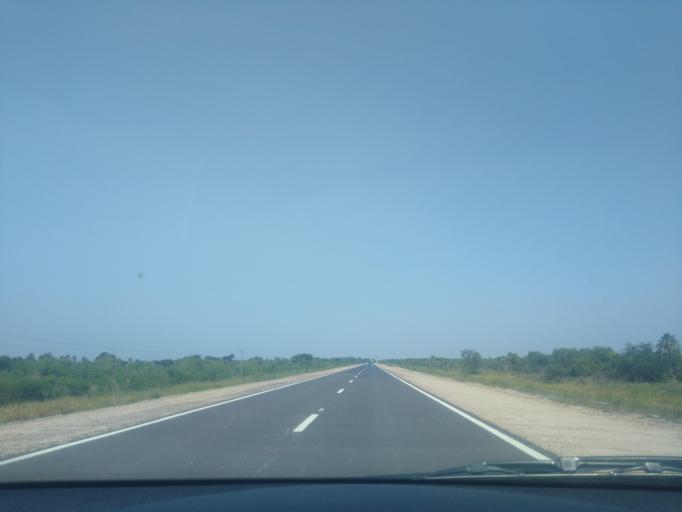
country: AR
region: Chaco
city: Puerto Tirol
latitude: -27.5705
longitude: -59.2684
